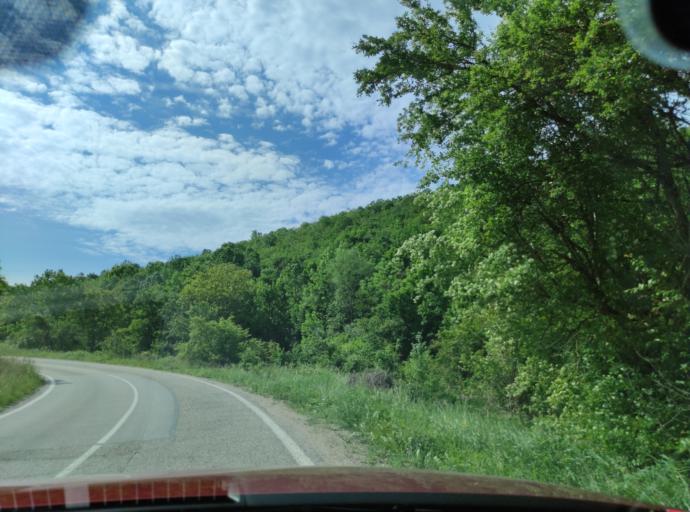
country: BG
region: Montana
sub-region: Obshtina Chiprovtsi
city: Chiprovtsi
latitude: 43.4915
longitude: 22.8041
